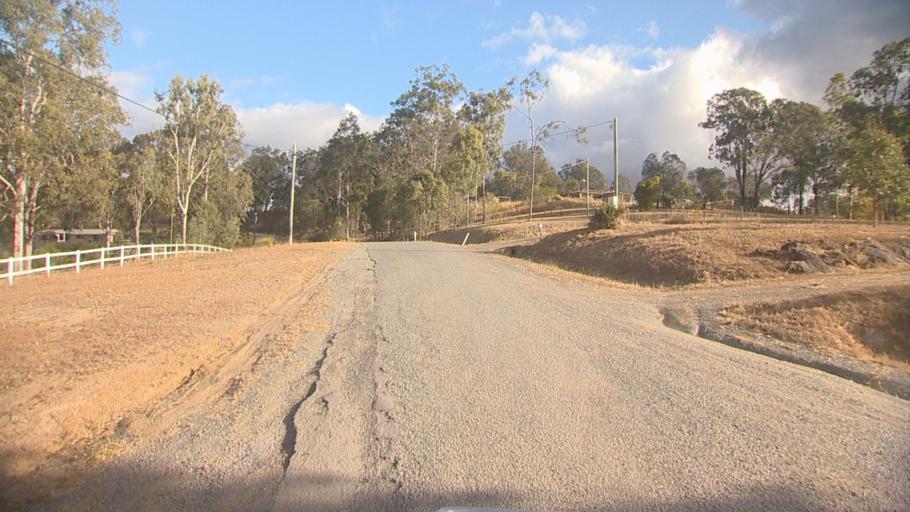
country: AU
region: Queensland
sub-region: Logan
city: Cedar Vale
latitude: -27.8973
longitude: 153.0717
